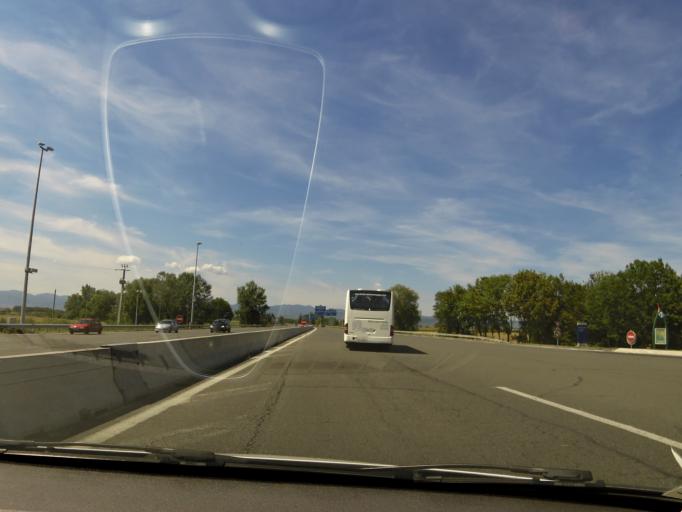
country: FR
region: Auvergne
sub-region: Departement du Puy-de-Dome
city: Pont-du-Chateau
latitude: 45.8280
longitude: 3.2401
